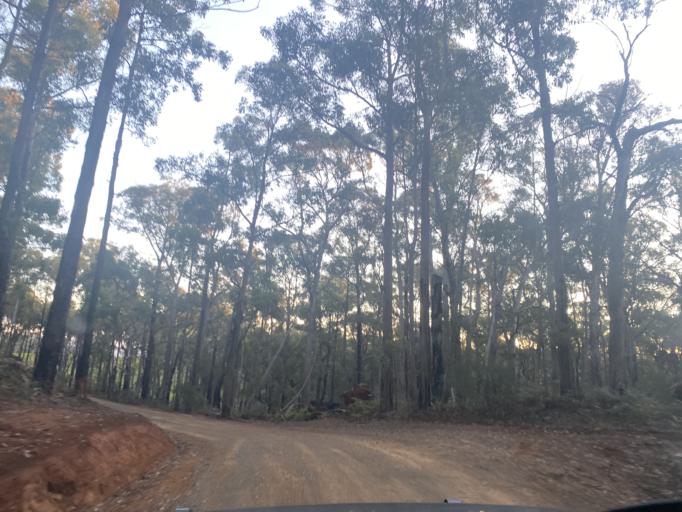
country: AU
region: Victoria
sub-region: Yarra Ranges
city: Healesville
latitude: -37.4226
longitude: 145.5263
